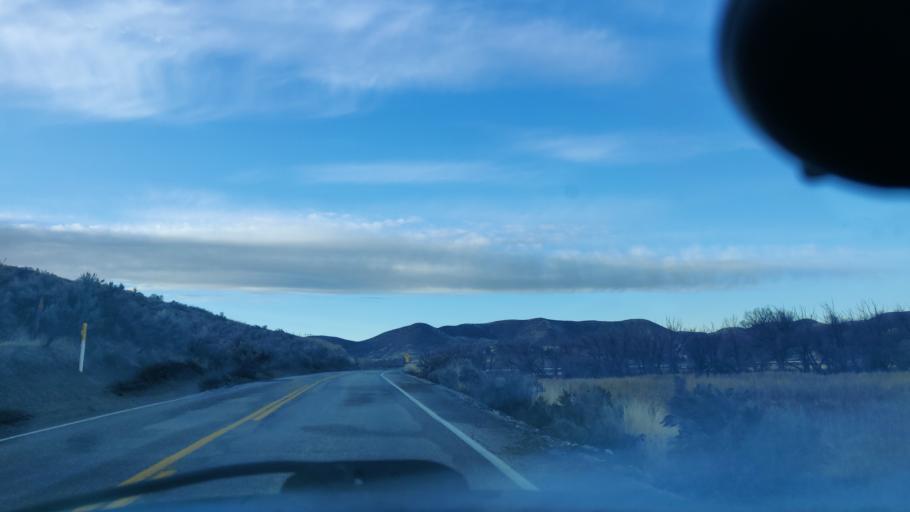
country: US
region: Idaho
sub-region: Ada County
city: Eagle
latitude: 43.7292
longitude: -116.2828
